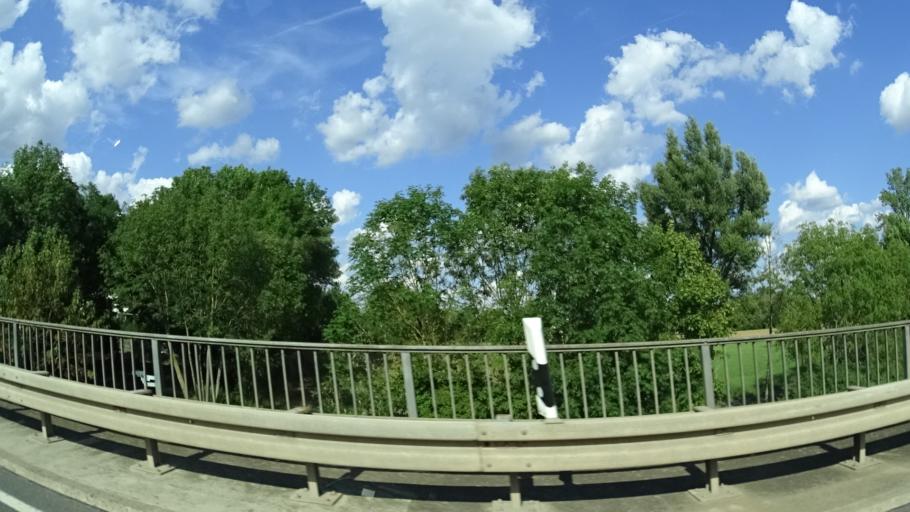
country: DE
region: Bavaria
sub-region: Regierungsbezirk Unterfranken
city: Bad Konigshofen im Grabfeld
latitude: 50.2962
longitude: 10.4642
